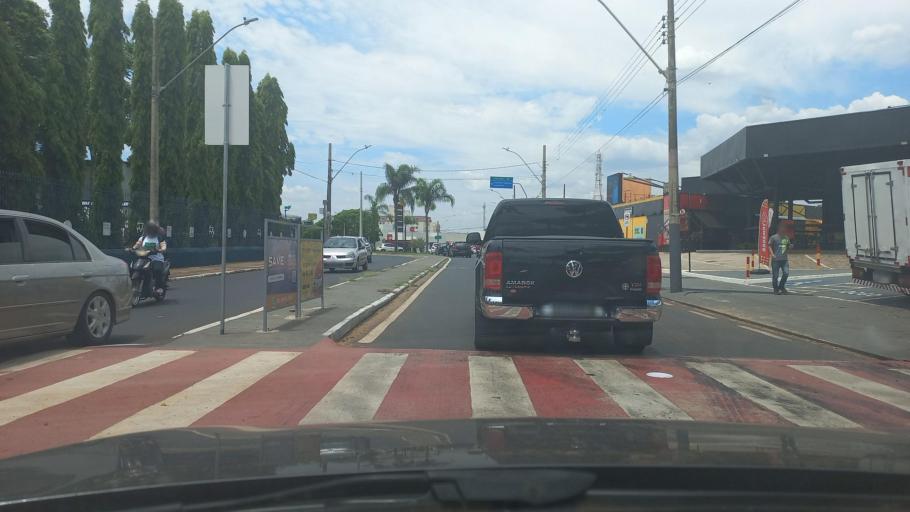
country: BR
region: Minas Gerais
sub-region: Uberaba
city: Uberaba
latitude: -19.7704
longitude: -47.9461
